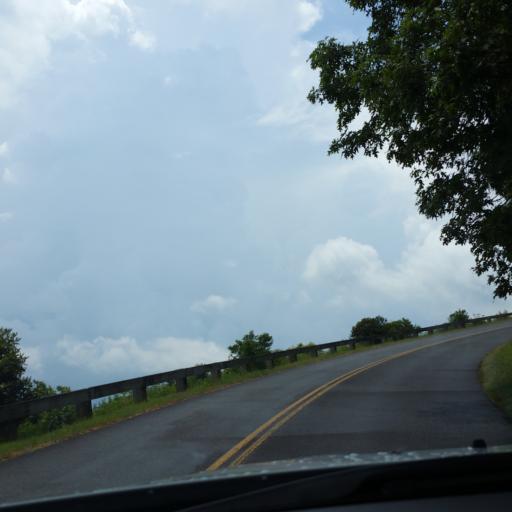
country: US
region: North Carolina
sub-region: Transylvania County
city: Brevard
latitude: 35.3162
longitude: -82.8300
